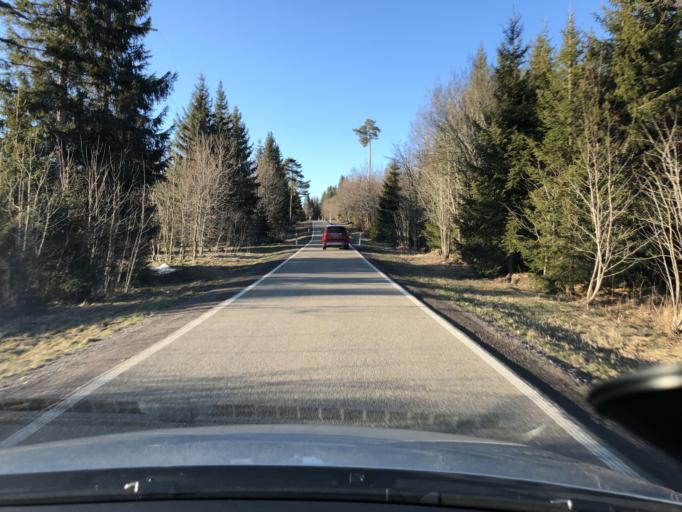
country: DE
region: Baden-Wuerttemberg
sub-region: Freiburg Region
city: Schluchsee
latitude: 47.8242
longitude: 8.2093
